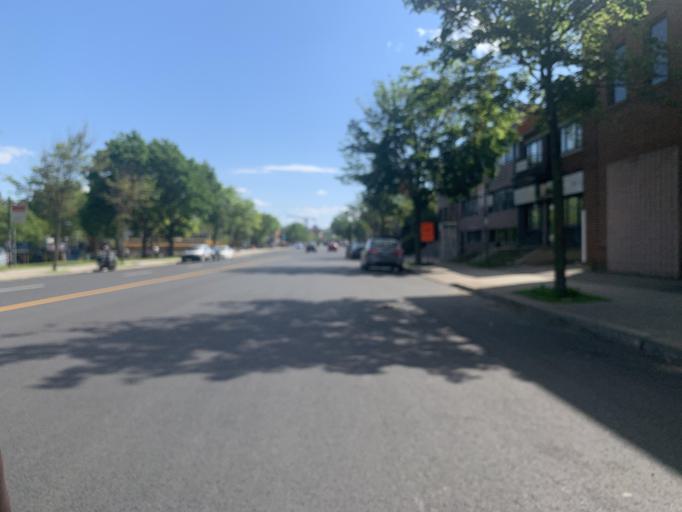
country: CA
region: Quebec
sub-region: Monteregie
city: Longueuil
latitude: 45.5429
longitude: -73.5540
